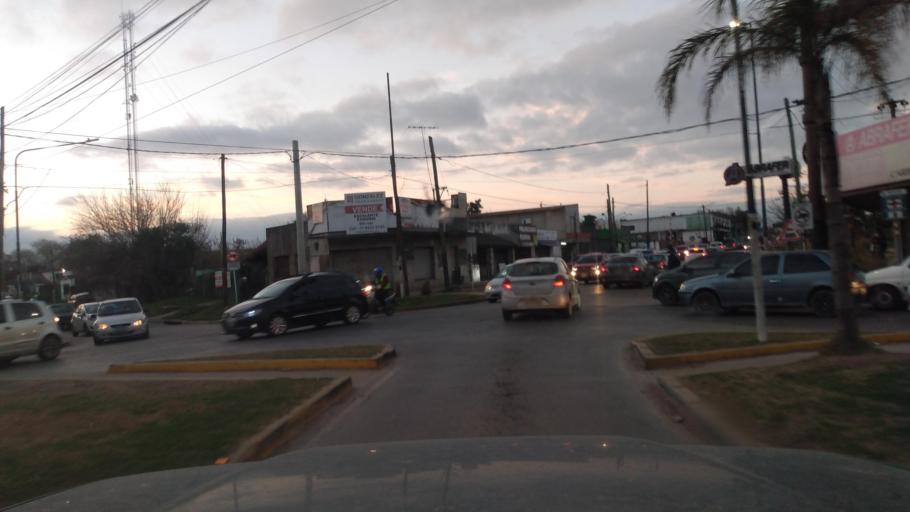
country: AR
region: Buenos Aires
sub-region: Partido de Pilar
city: Pilar
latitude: -34.4672
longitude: -58.9158
